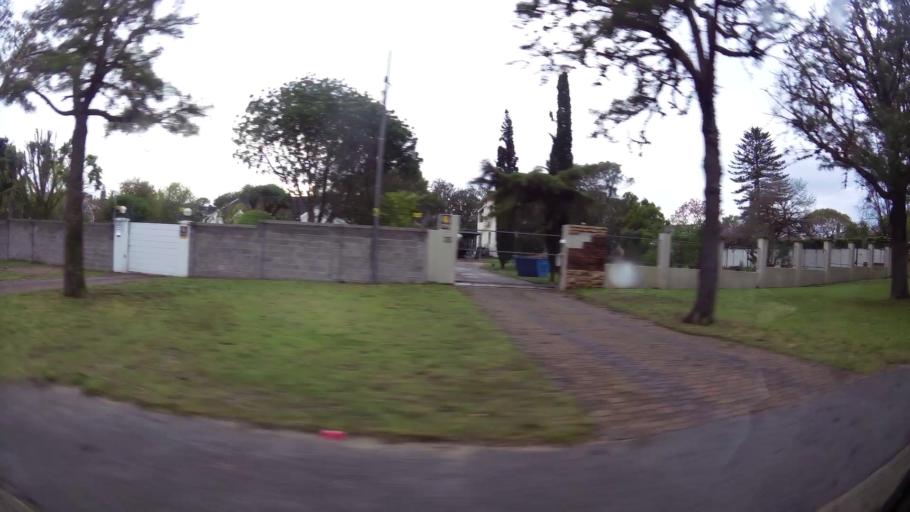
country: ZA
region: Eastern Cape
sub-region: Nelson Mandela Bay Metropolitan Municipality
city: Port Elizabeth
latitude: -33.9742
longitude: 25.5802
